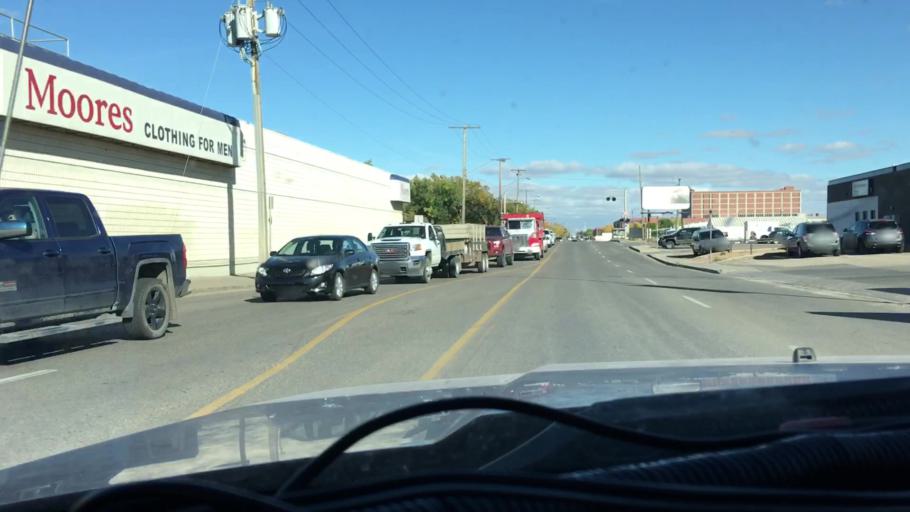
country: CA
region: Saskatchewan
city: Regina
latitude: 50.4629
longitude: -104.6172
